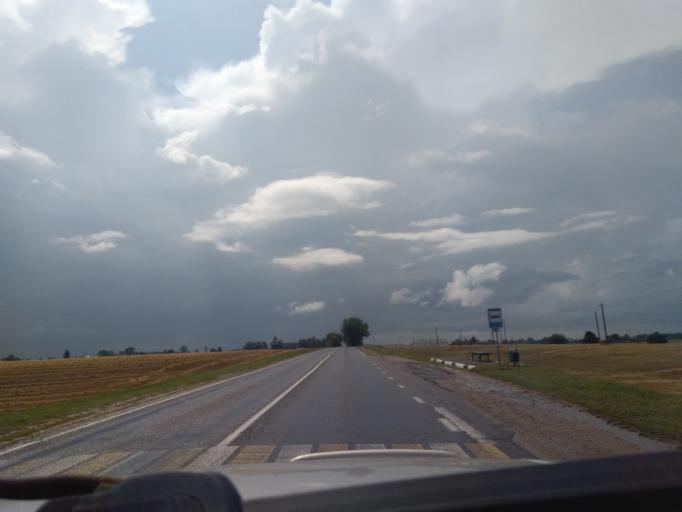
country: BY
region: Minsk
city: Tsimkavichy
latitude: 53.0972
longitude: 27.0410
